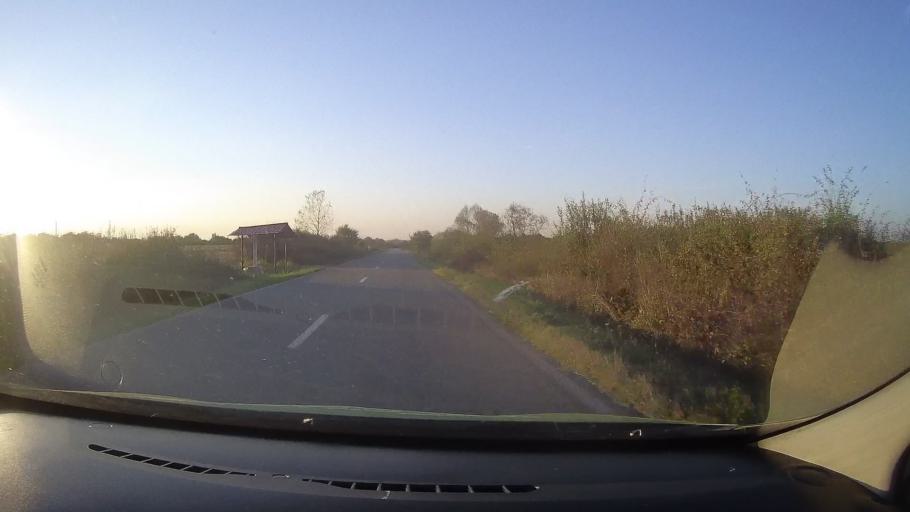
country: RO
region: Timis
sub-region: Comuna Traian Vuia
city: Traian Vuia
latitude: 45.7885
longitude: 22.0775
